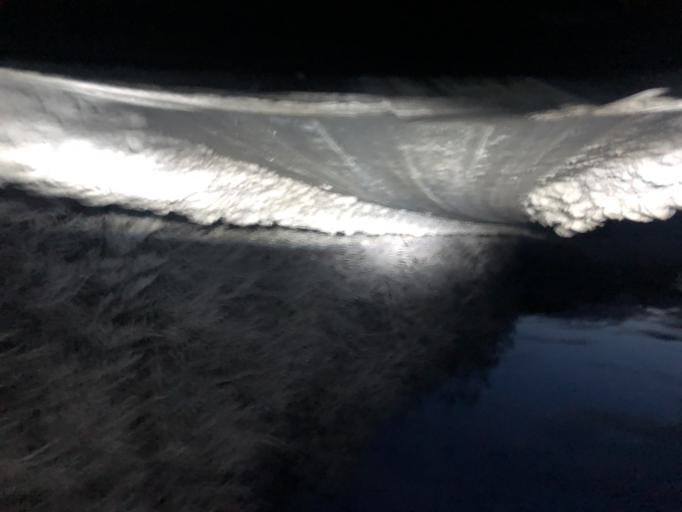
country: SE
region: Vaesternorrland
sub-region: Kramfors Kommun
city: Bollstabruk
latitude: 63.0551
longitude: 17.6672
